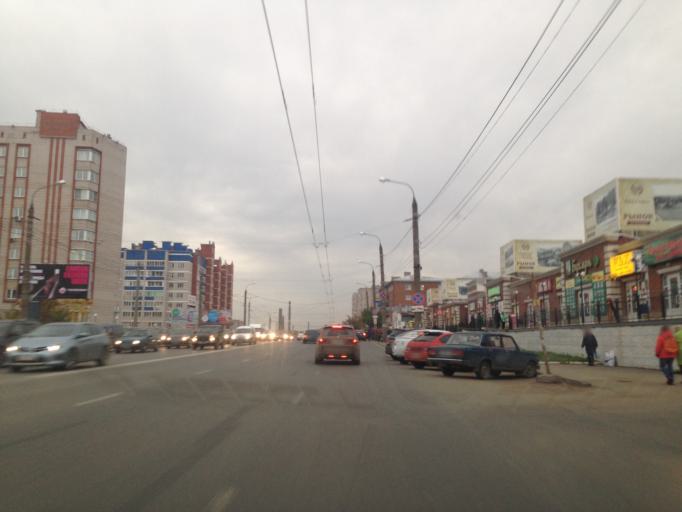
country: RU
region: Udmurtiya
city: Izhevsk
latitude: 56.8378
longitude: 53.2134
